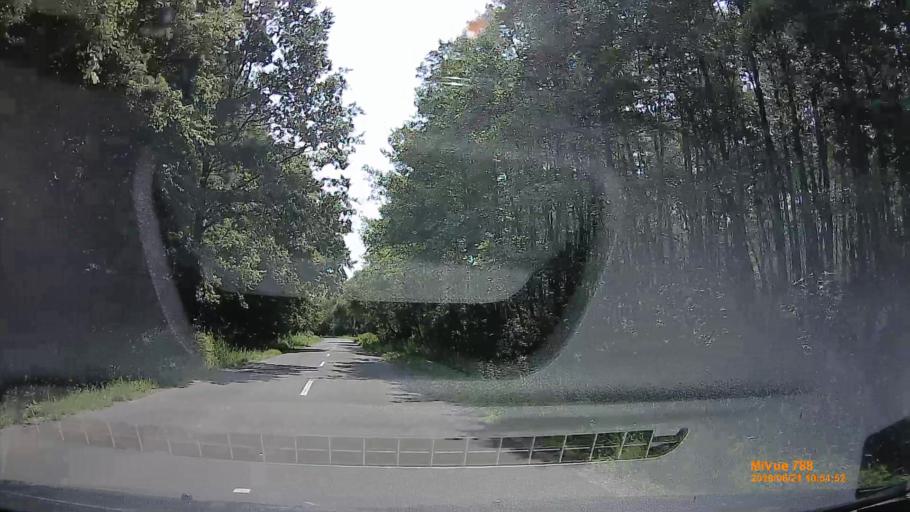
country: HU
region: Baranya
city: Buekkoesd
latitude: 46.1543
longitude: 18.0722
